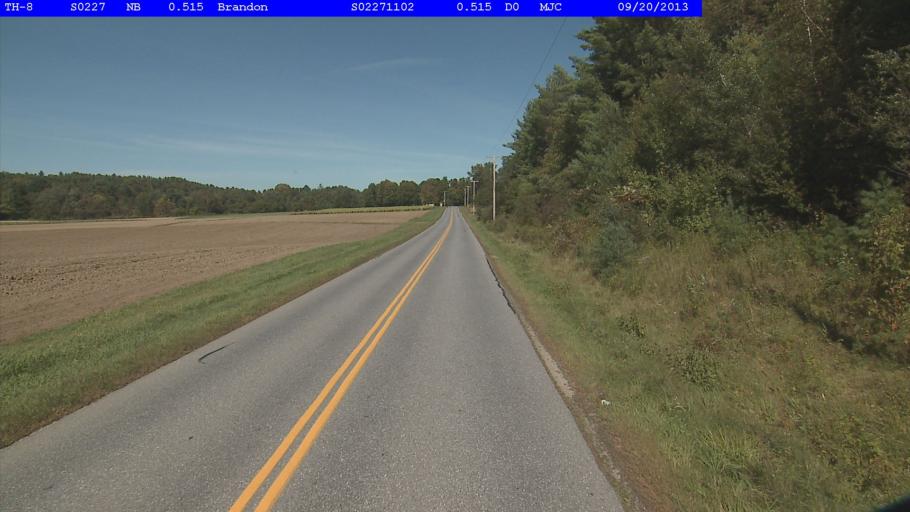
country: US
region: Vermont
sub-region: Rutland County
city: Brandon
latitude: 43.7818
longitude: -73.0528
